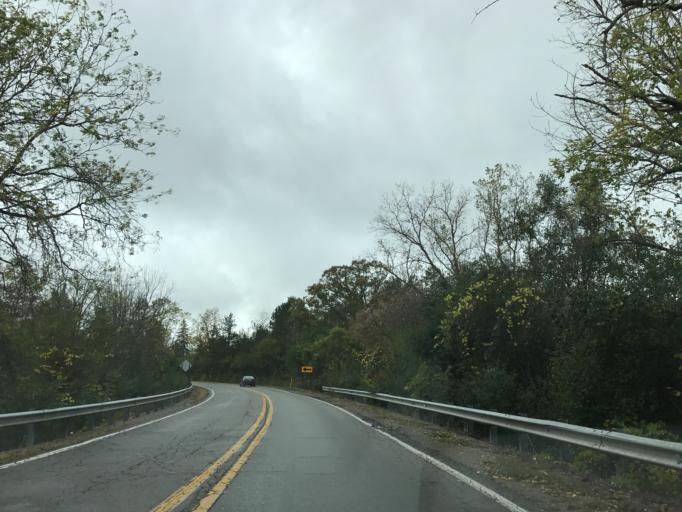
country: US
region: Michigan
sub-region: Washtenaw County
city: Ann Arbor
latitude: 42.2630
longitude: -83.6791
